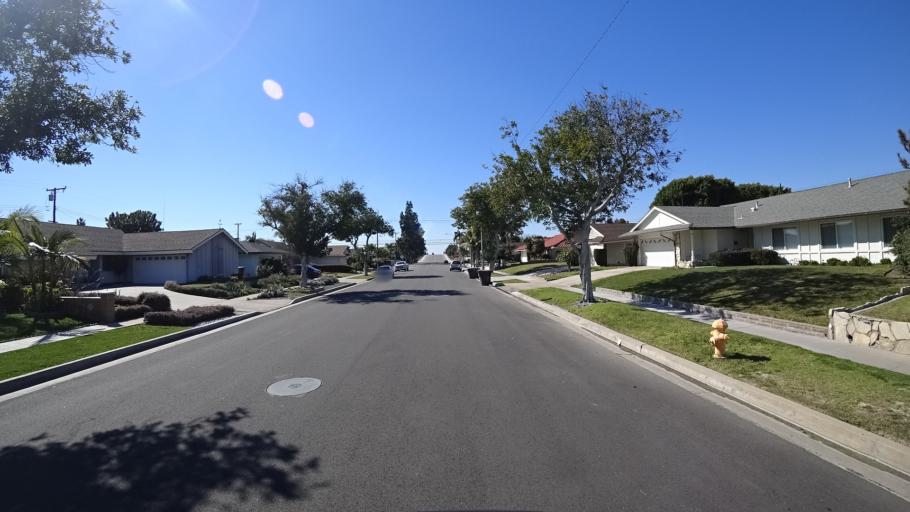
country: US
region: California
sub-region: Orange County
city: Placentia
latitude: 33.8327
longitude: -117.8704
